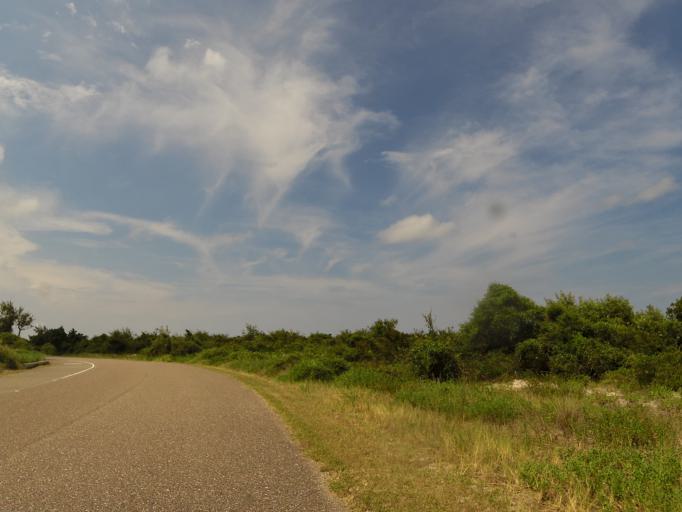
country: US
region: Florida
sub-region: Duval County
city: Atlantic Beach
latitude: 30.4391
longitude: -81.4136
